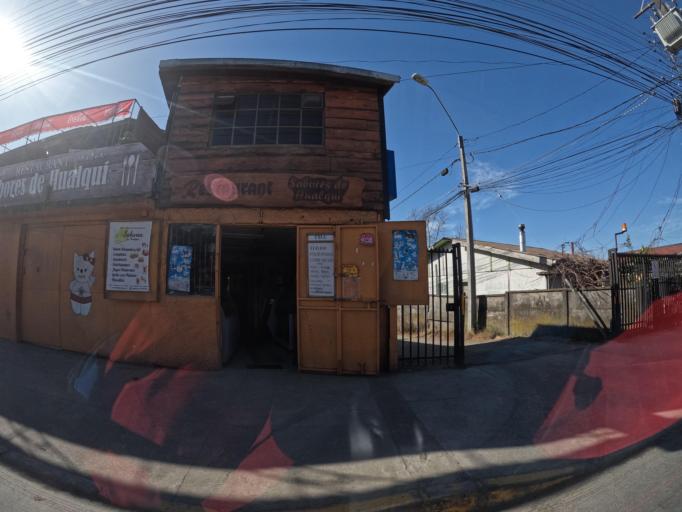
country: CL
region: Biobio
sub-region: Provincia de Concepcion
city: Chiguayante
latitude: -36.9720
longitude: -72.9378
